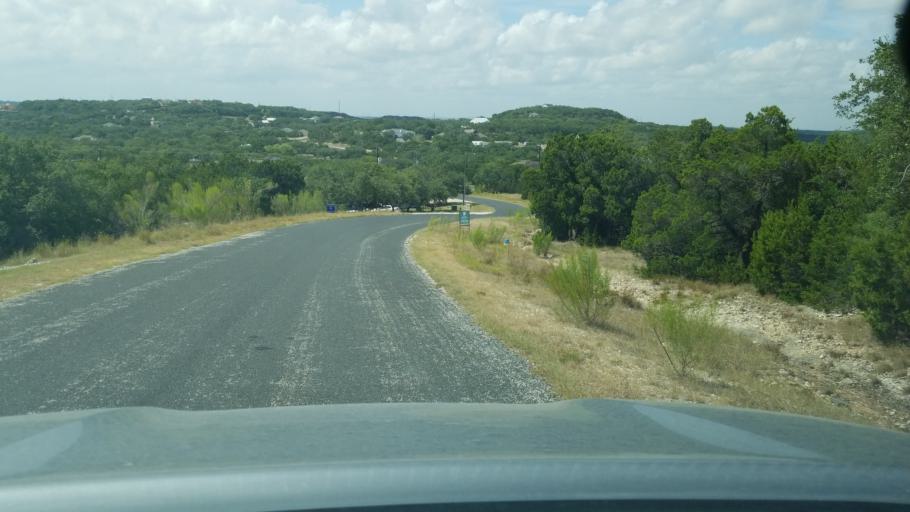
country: US
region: Texas
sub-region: Bexar County
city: Timberwood Park
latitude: 29.6813
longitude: -98.5114
